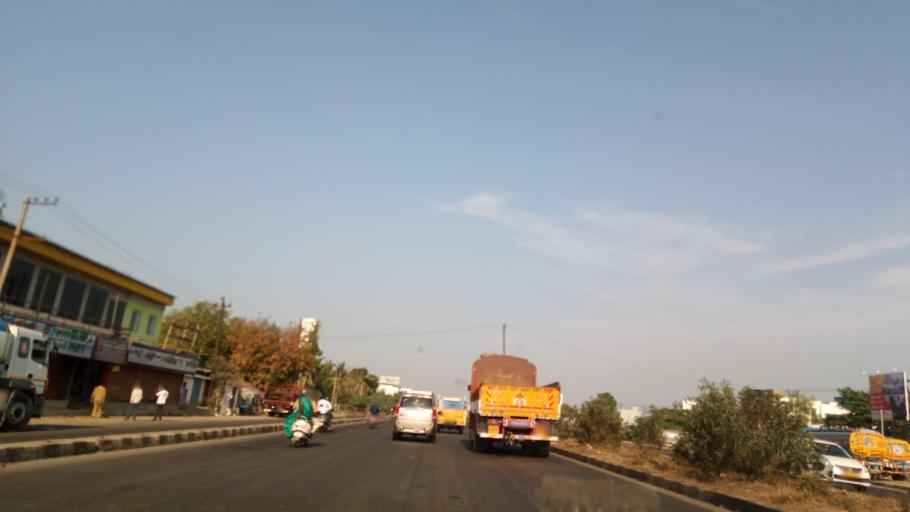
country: IN
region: Tamil Nadu
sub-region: Kancheepuram
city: Poonamalle
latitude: 13.0573
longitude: 80.1046
